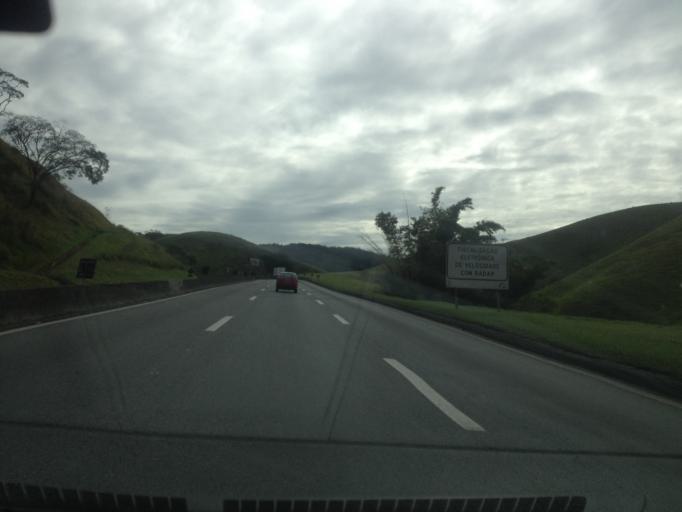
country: BR
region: Rio de Janeiro
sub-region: Pirai
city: Pirai
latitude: -22.6121
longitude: -43.9315
